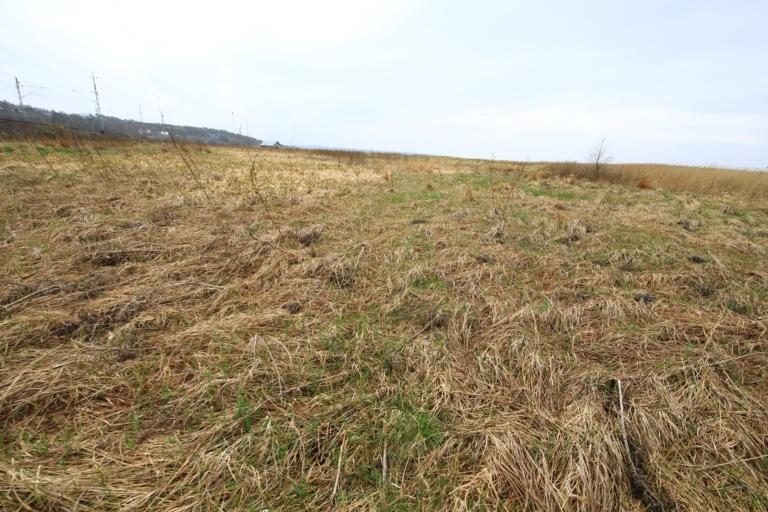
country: SE
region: Halland
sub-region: Kungsbacka Kommun
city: Frillesas
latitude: 57.3108
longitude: 12.1705
